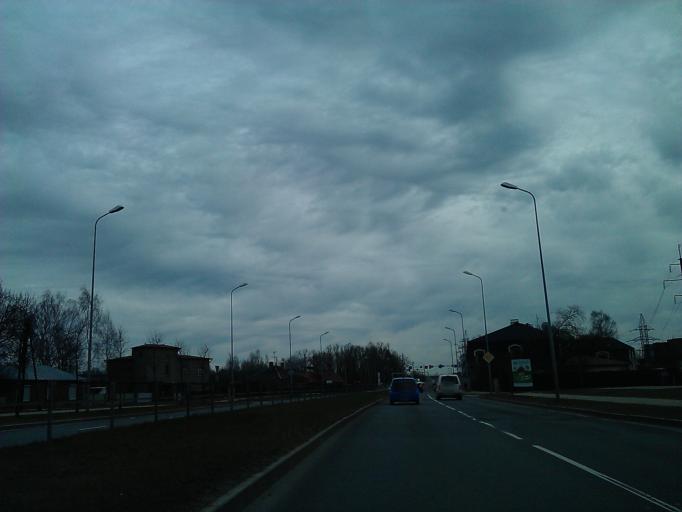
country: LV
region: Riga
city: Riga
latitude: 56.9414
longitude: 24.1702
